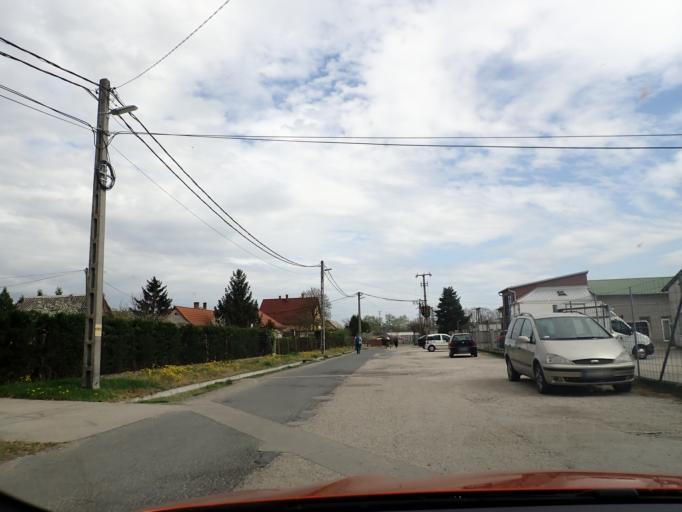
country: HU
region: Tolna
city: Paks
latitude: 46.6061
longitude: 18.8456
